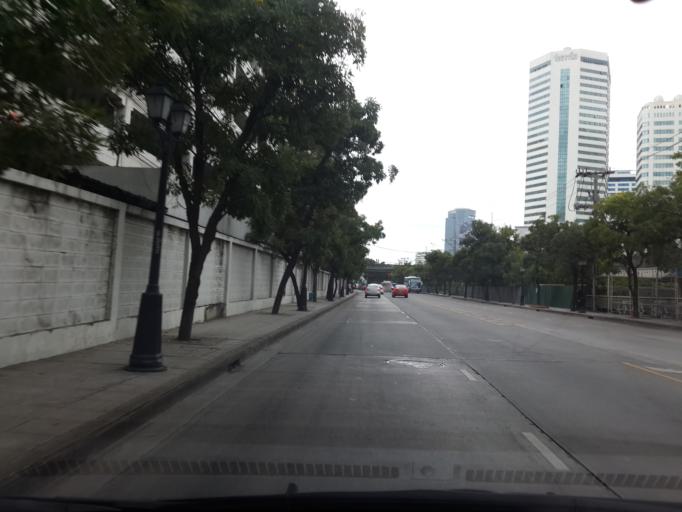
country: TH
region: Bangkok
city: Huai Khwang
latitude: 13.7576
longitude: 100.5728
